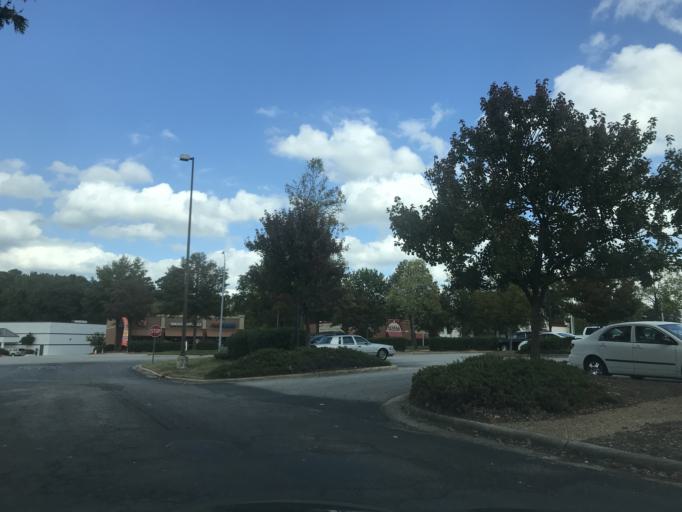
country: US
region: North Carolina
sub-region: Wake County
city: Garner
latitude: 35.7243
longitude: -78.6530
